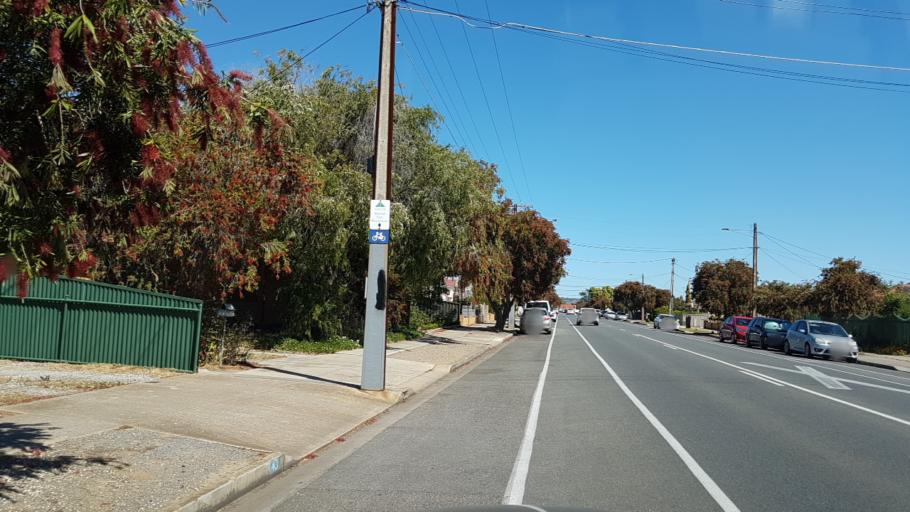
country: AU
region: South Australia
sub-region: Marion
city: South Plympton
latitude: -34.9635
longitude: 138.5636
